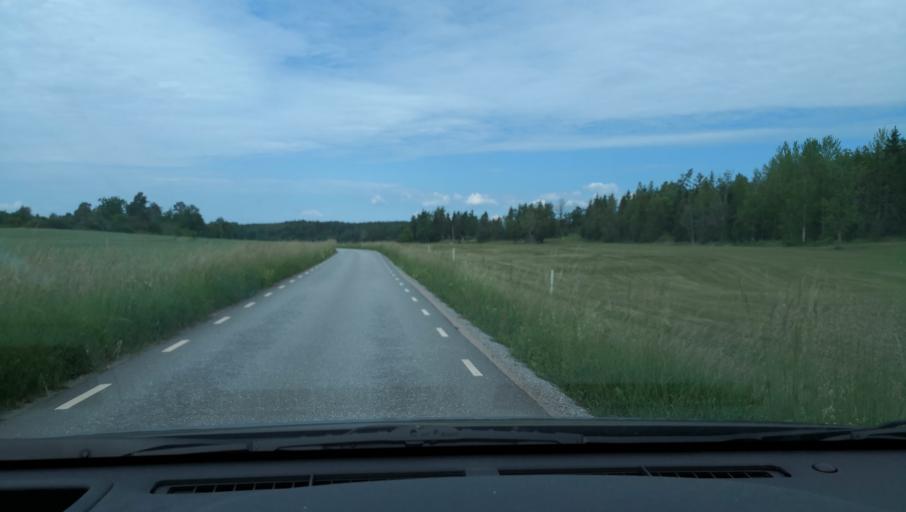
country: SE
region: Uppsala
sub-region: Habo Kommun
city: Balsta
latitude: 59.6990
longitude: 17.4790
